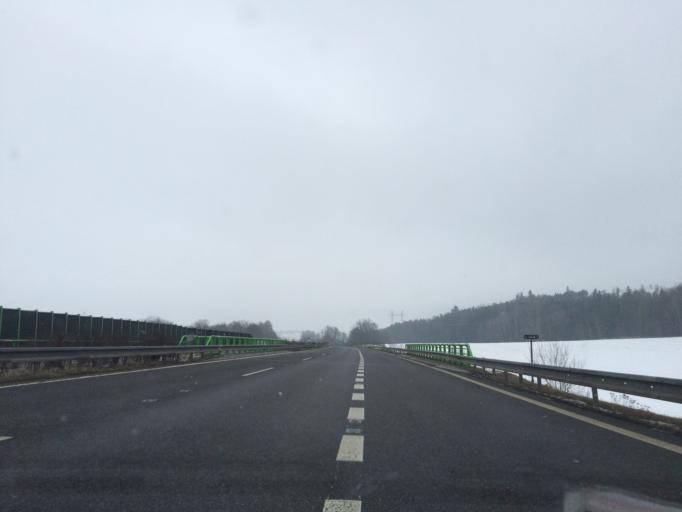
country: CZ
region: Jihocesky
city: Mirotice
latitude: 49.3559
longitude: 14.0553
